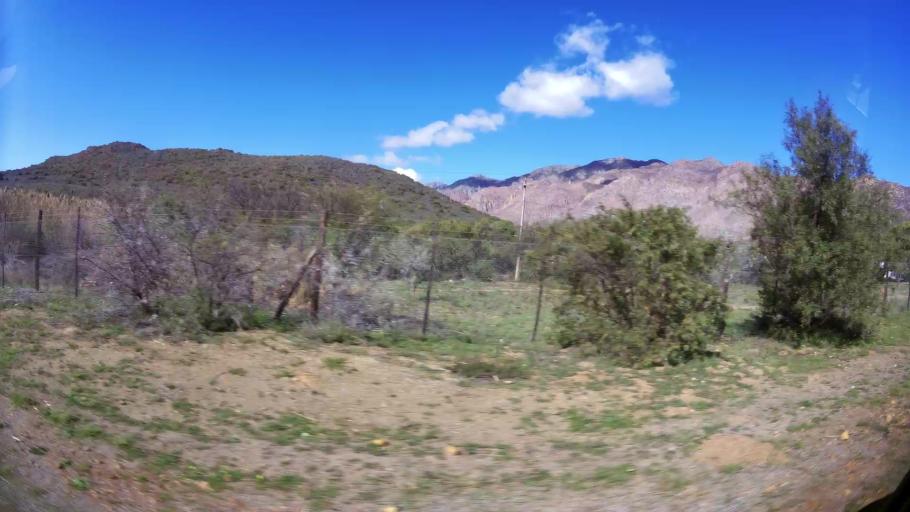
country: ZA
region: Western Cape
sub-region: Cape Winelands District Municipality
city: Ashton
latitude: -33.7914
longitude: 20.1286
